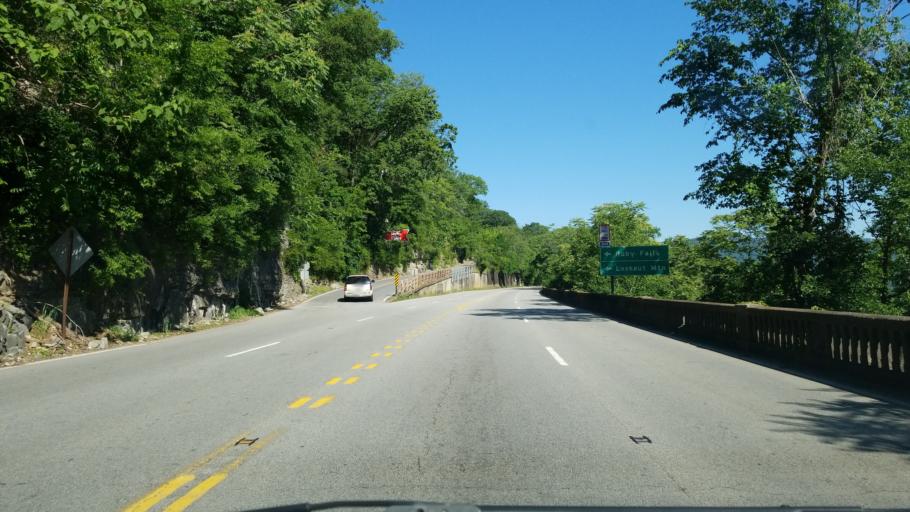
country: US
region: Tennessee
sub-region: Hamilton County
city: Lookout Mountain
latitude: 35.0205
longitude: -85.3383
